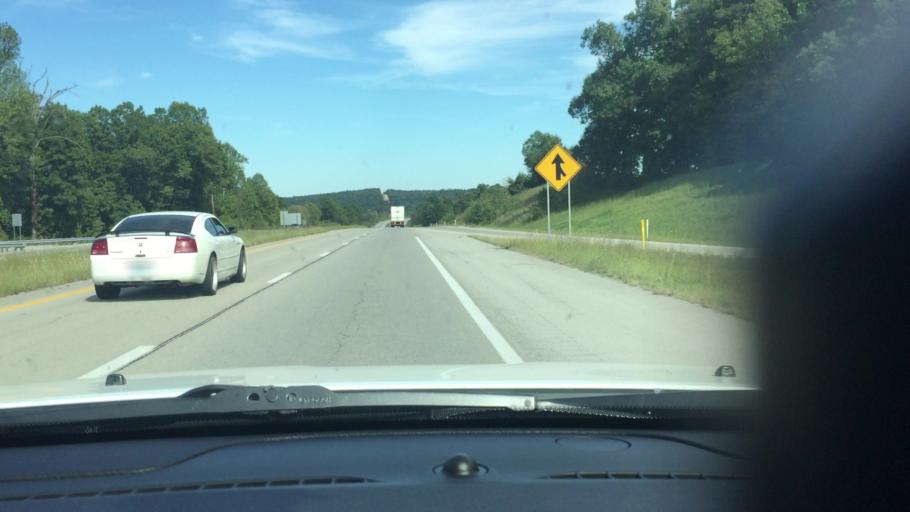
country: US
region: Kentucky
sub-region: Caldwell County
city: Princeton
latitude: 37.1339
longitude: -87.8676
